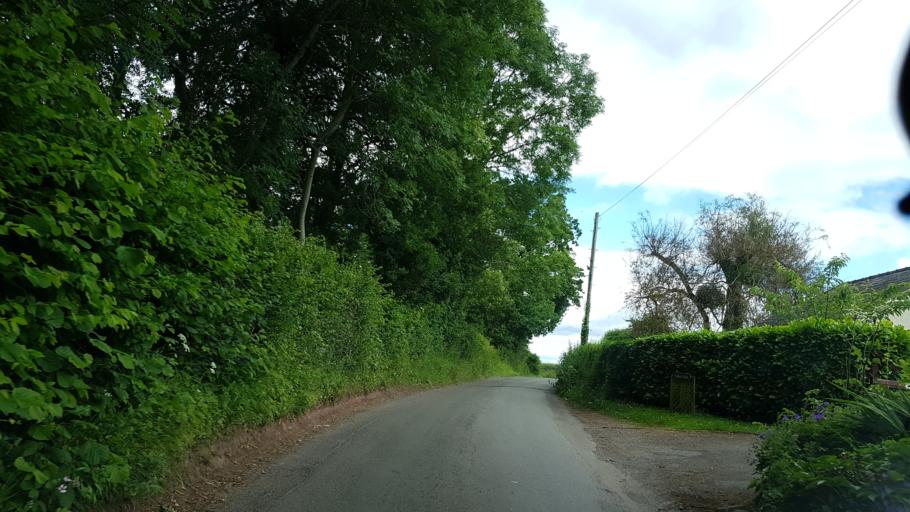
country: GB
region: Wales
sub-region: Monmouthshire
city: Llanarth
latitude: 51.7883
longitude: -2.8286
